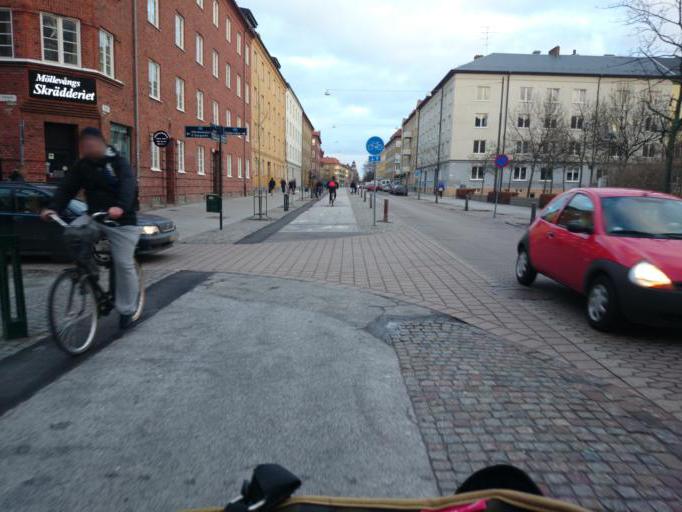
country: SE
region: Skane
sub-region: Malmo
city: Malmoe
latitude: 55.5909
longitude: 13.0107
